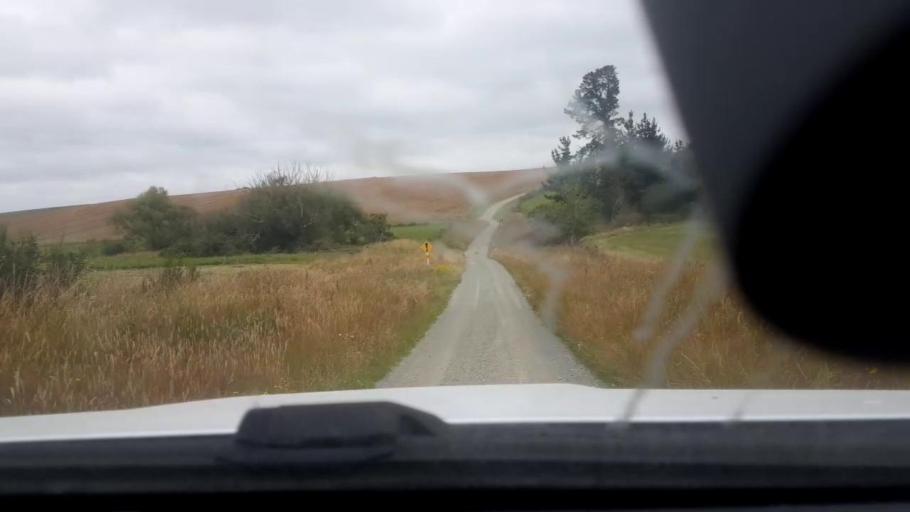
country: NZ
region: Canterbury
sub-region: Timaru District
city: Pleasant Point
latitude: -44.2003
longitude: 171.1870
